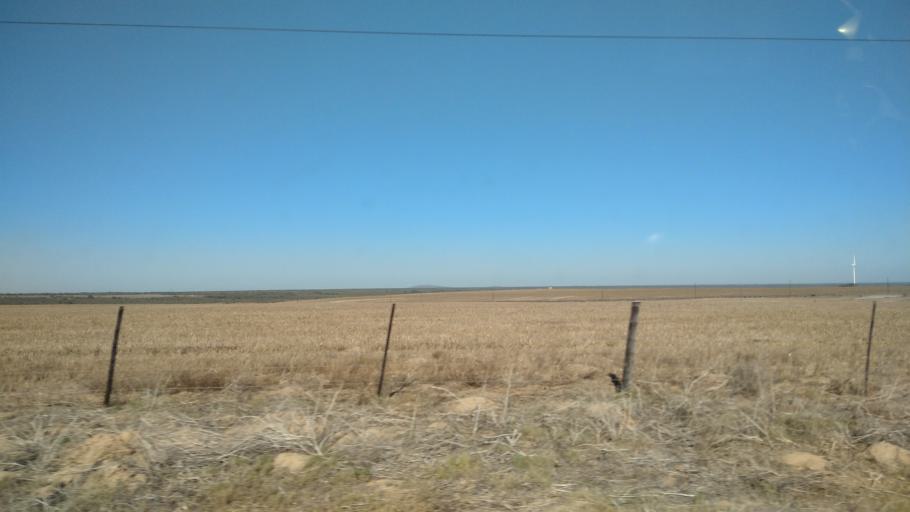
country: ZA
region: Western Cape
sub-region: West Coast District Municipality
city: Moorreesburg
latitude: -33.1022
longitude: 18.4237
